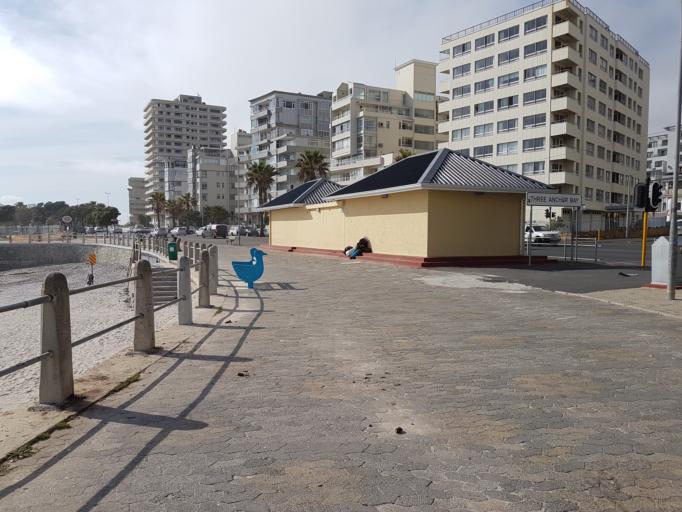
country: ZA
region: Western Cape
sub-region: City of Cape Town
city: Cape Town
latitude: -33.9089
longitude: 18.3932
